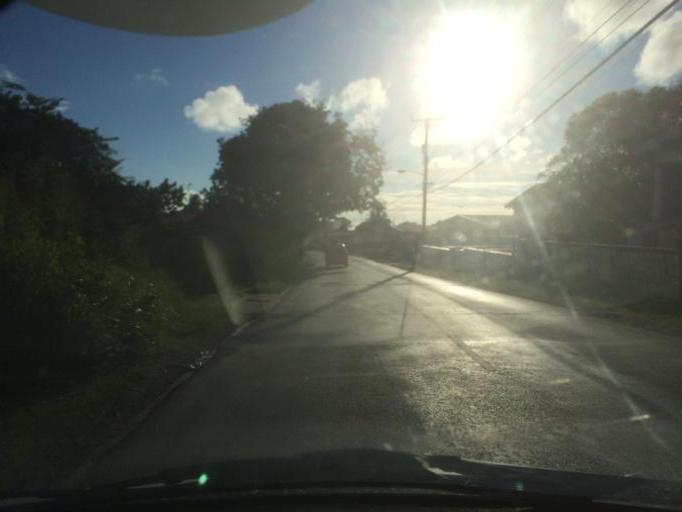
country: BB
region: Christ Church
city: Oistins
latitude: 13.0779
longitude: -59.5348
